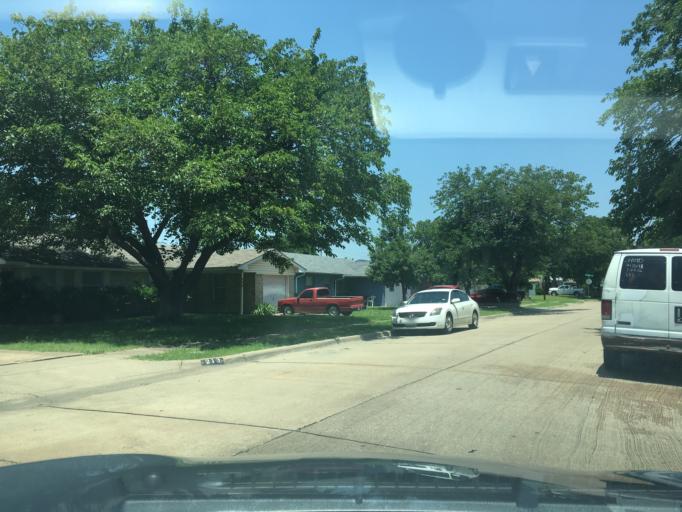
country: US
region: Texas
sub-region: Dallas County
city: Richardson
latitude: 32.9121
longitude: -96.6997
